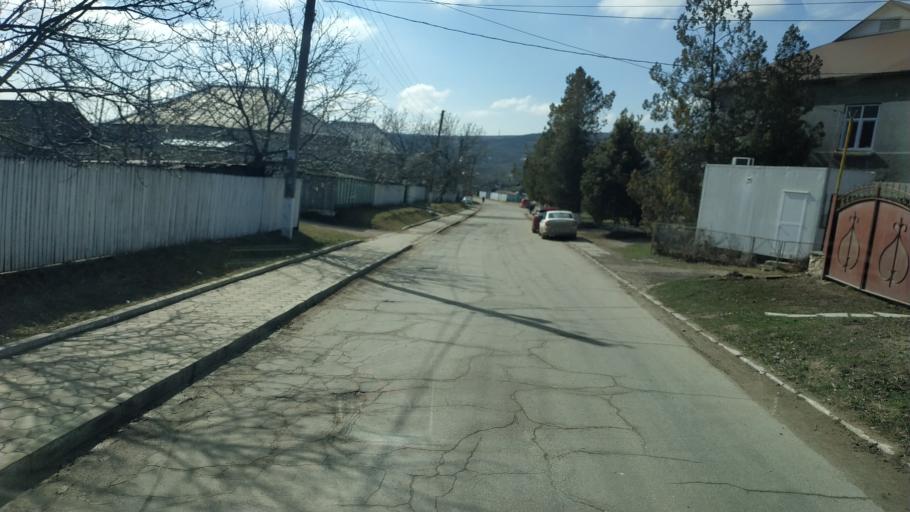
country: MD
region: Straseni
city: Straseni
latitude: 47.0165
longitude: 28.5440
